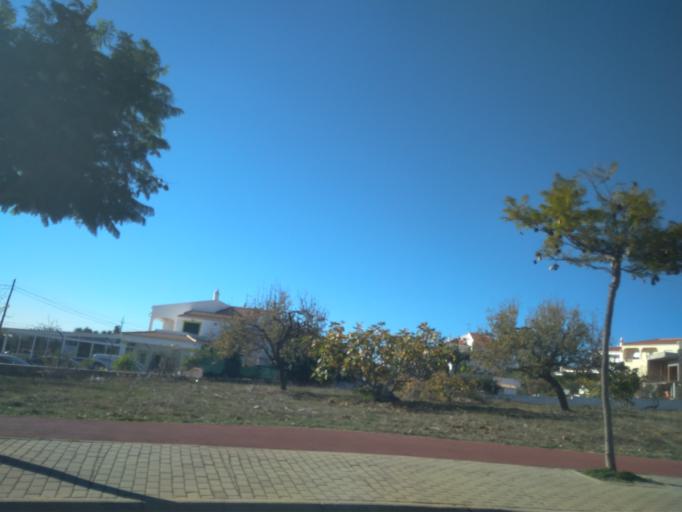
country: PT
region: Faro
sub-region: Albufeira
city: Ferreiras
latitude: 37.1153
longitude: -8.2297
